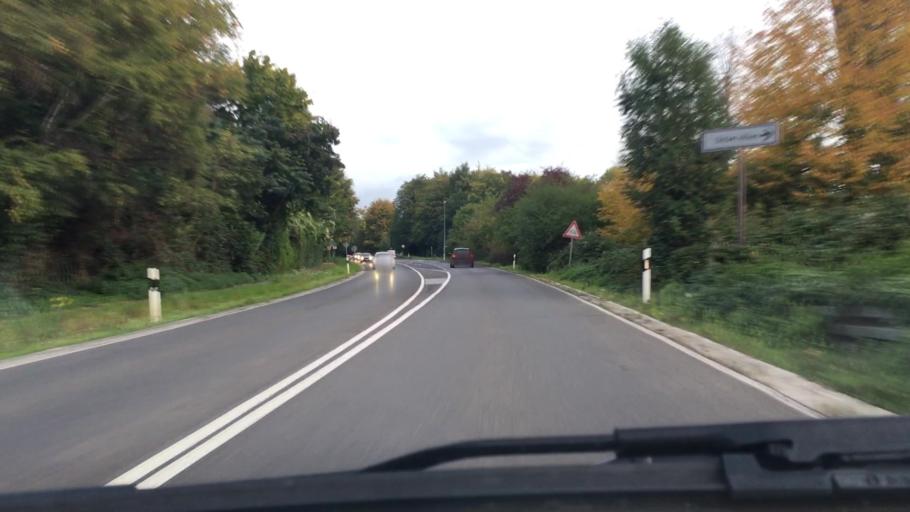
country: DE
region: North Rhine-Westphalia
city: Wesseling
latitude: 50.8592
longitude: 6.9981
